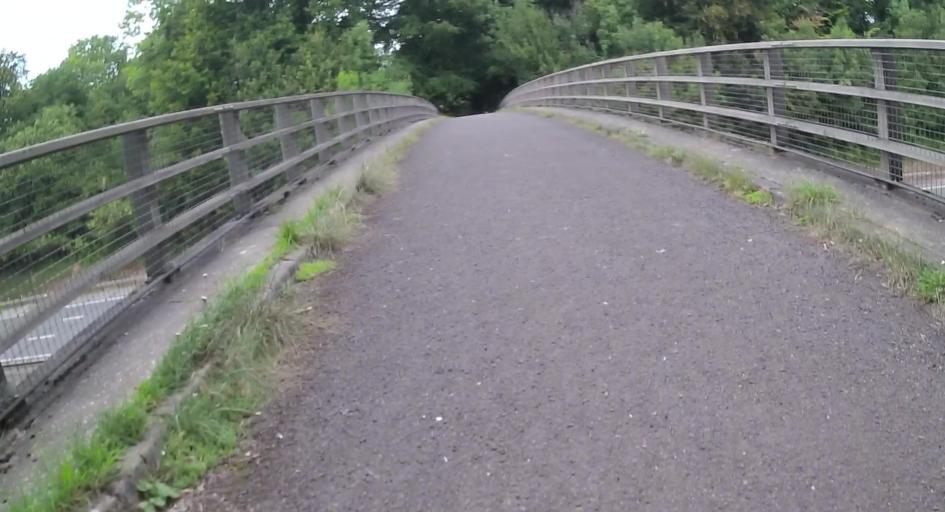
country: GB
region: England
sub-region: Hampshire
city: Basingstoke
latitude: 51.2217
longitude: -1.1457
